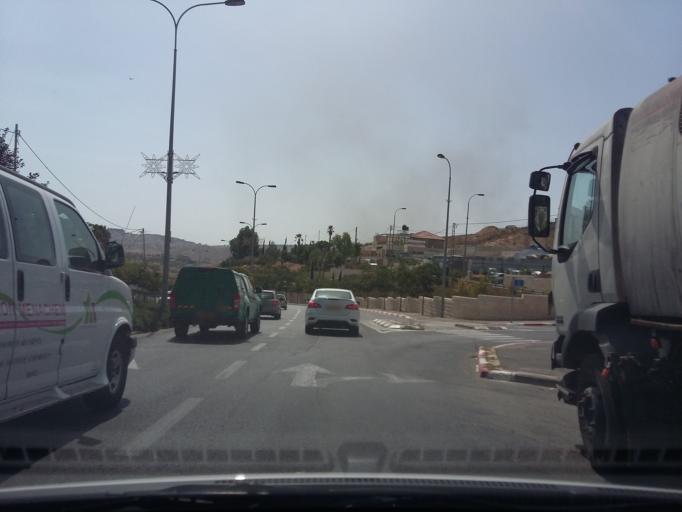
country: PS
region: West Bank
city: Ar Ram wa Dahiyat al Barid
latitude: 31.8298
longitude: 35.2215
